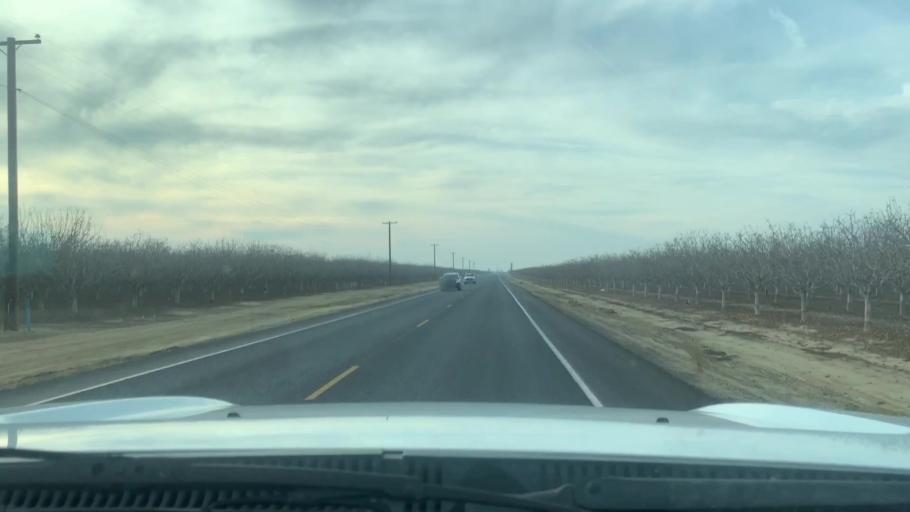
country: US
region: California
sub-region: Kern County
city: Lost Hills
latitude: 35.4993
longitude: -119.6299
